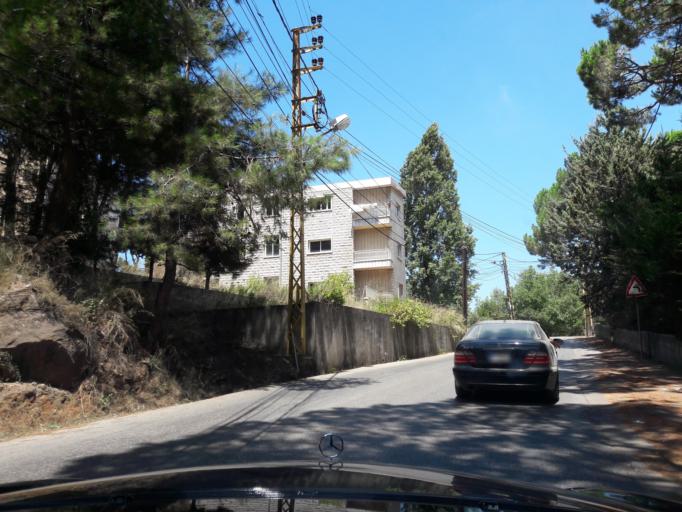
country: LB
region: Mont-Liban
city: Djounie
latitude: 33.9252
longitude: 35.6594
